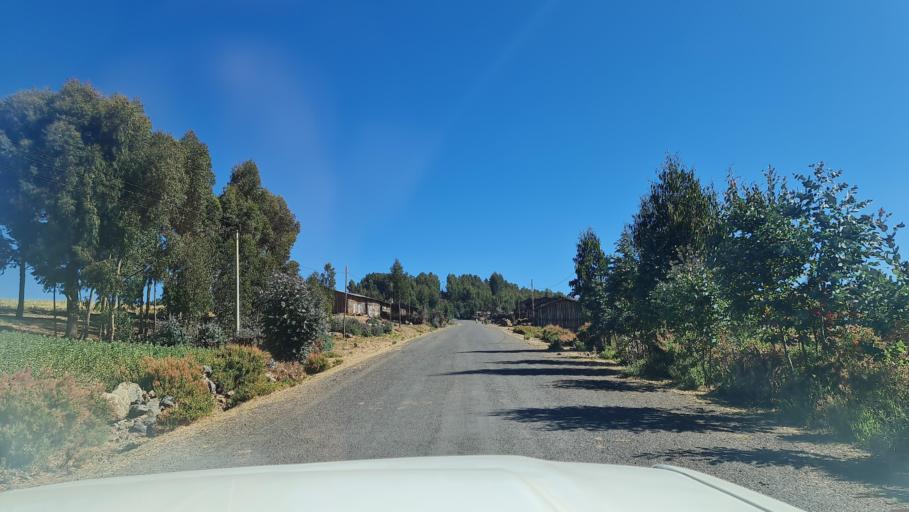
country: ET
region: Amhara
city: Debark'
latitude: 13.1068
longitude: 38.1472
